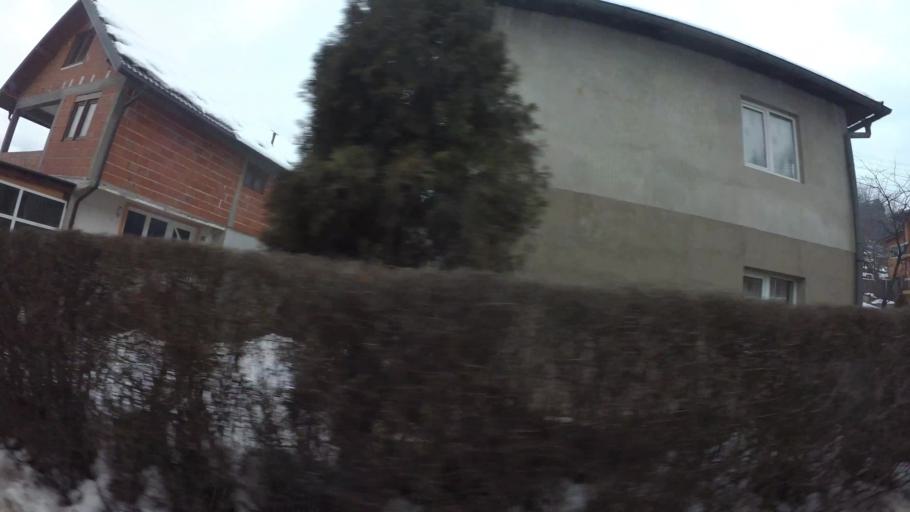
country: BA
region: Federation of Bosnia and Herzegovina
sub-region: Kanton Sarajevo
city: Sarajevo
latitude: 43.8531
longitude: 18.3540
